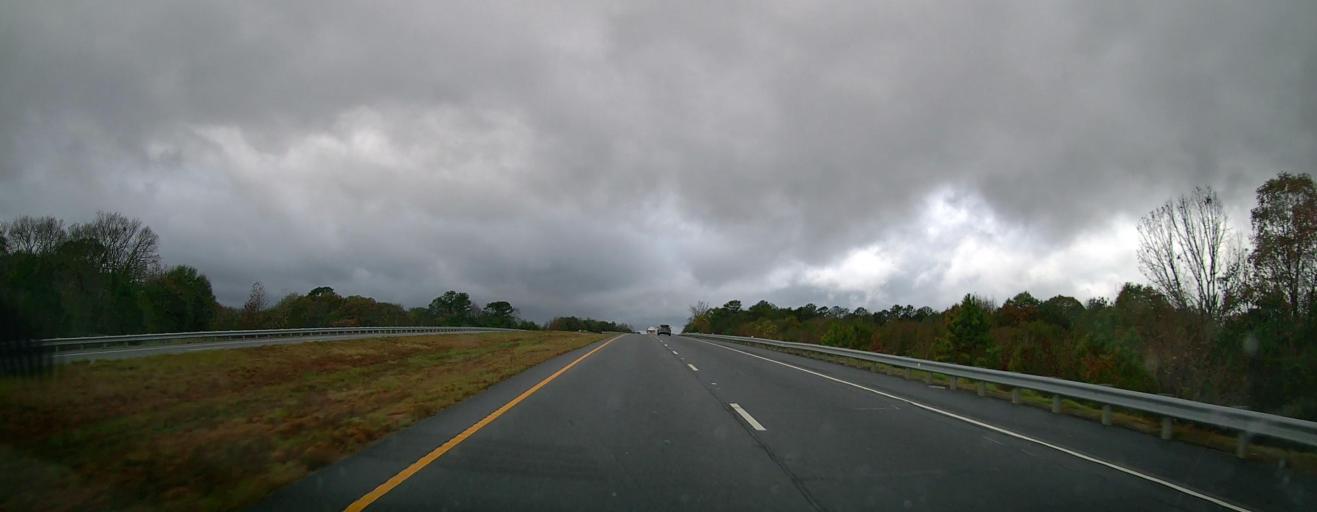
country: US
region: Georgia
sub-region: Jackson County
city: Nicholson
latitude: 34.0603
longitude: -83.4165
